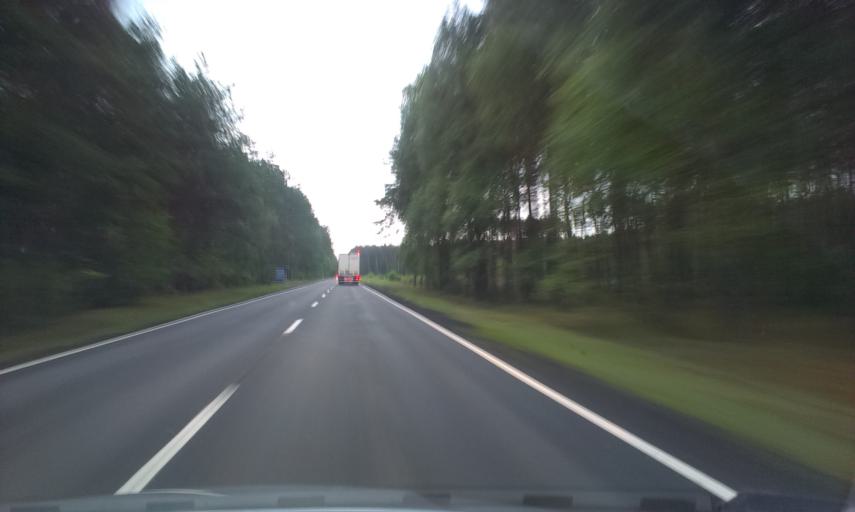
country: PL
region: Greater Poland Voivodeship
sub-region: Powiat zlotowski
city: Tarnowka
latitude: 53.3288
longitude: 16.7943
